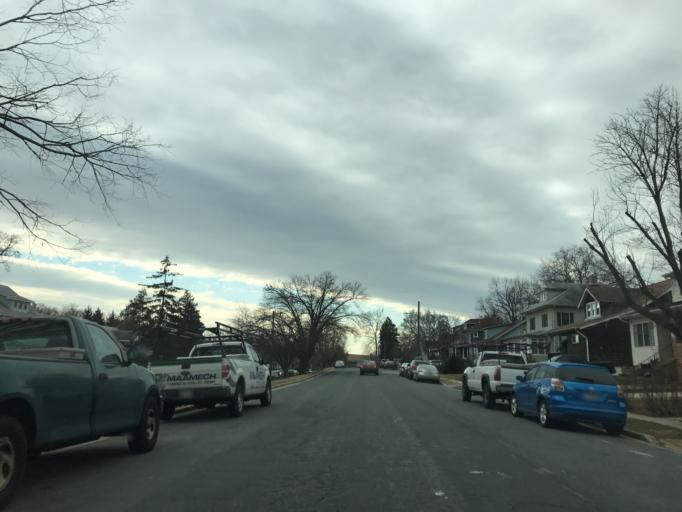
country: US
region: Maryland
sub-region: Baltimore County
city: Arbutus
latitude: 39.2456
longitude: -76.6940
